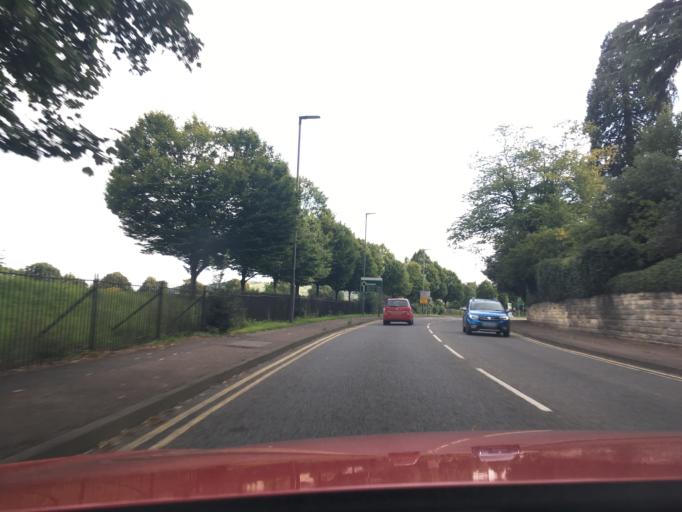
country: GB
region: England
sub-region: Gloucestershire
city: Cheltenham
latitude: 51.8895
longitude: -2.0671
